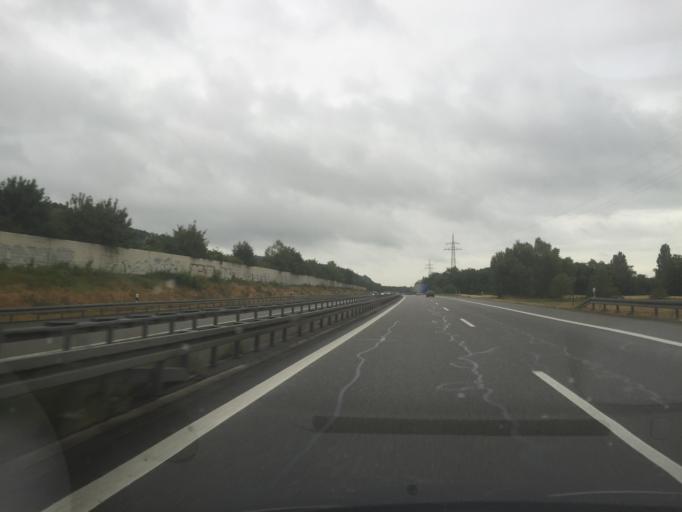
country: FR
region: Alsace
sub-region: Departement du Haut-Rhin
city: Kembs
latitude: 47.6894
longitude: 7.5209
